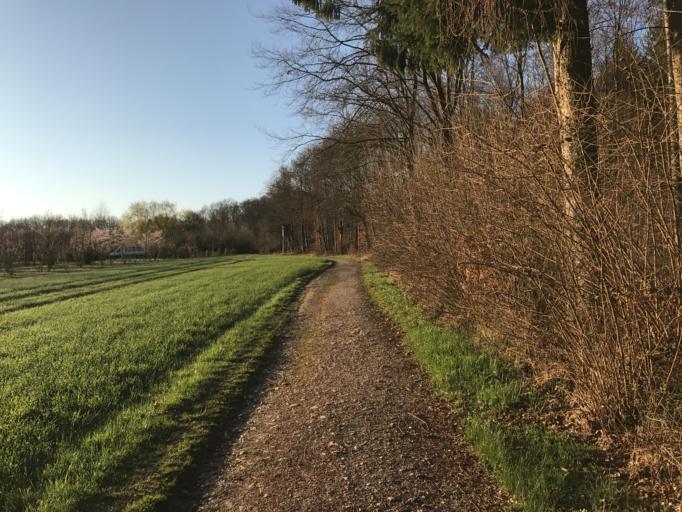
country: DE
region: Baden-Wuerttemberg
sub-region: Regierungsbezirk Stuttgart
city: Hochdorf
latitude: 48.6901
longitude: 9.4476
